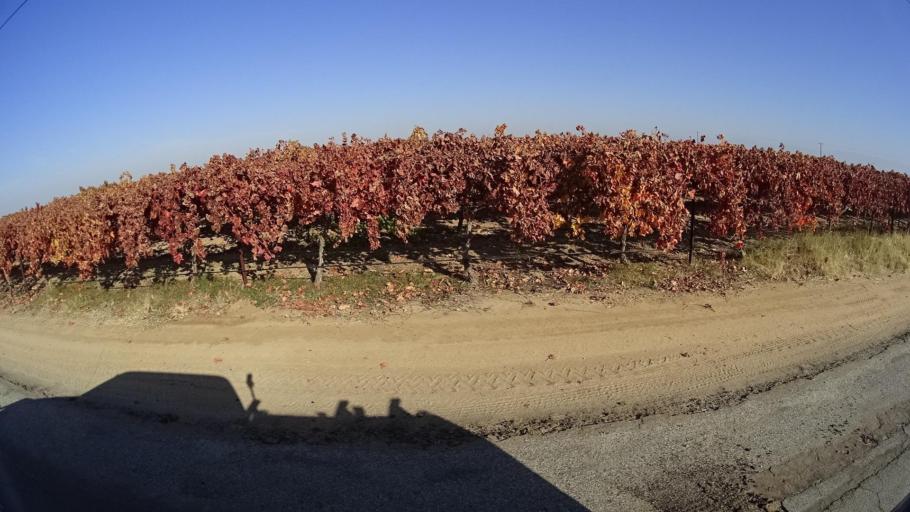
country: US
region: California
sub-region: Tulare County
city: Richgrove
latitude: 35.7471
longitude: -119.1532
